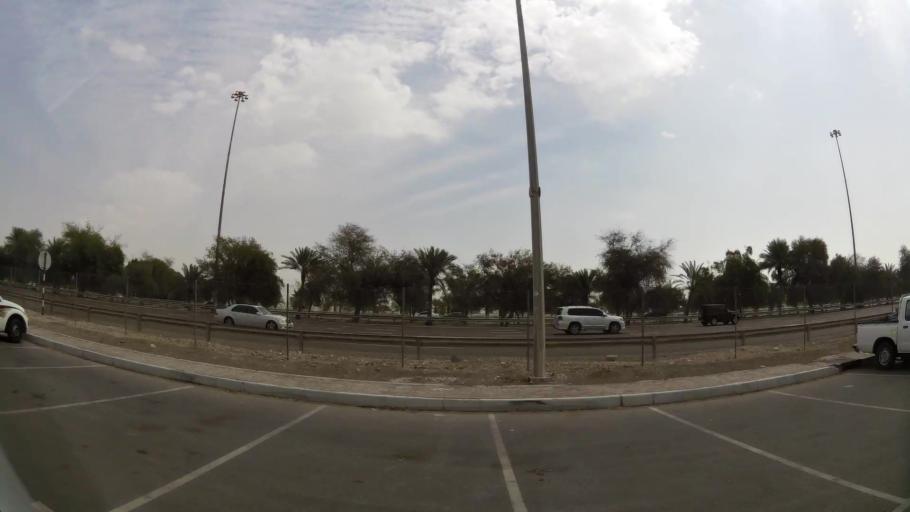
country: AE
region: Abu Dhabi
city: Abu Dhabi
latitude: 24.5246
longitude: 54.6912
